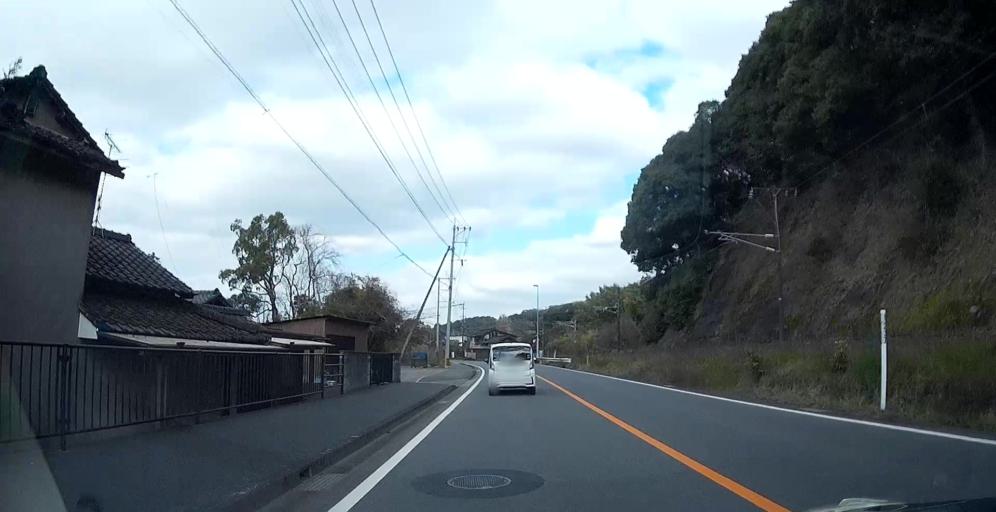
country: JP
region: Kumamoto
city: Yatsushiro
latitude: 32.4395
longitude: 130.5852
